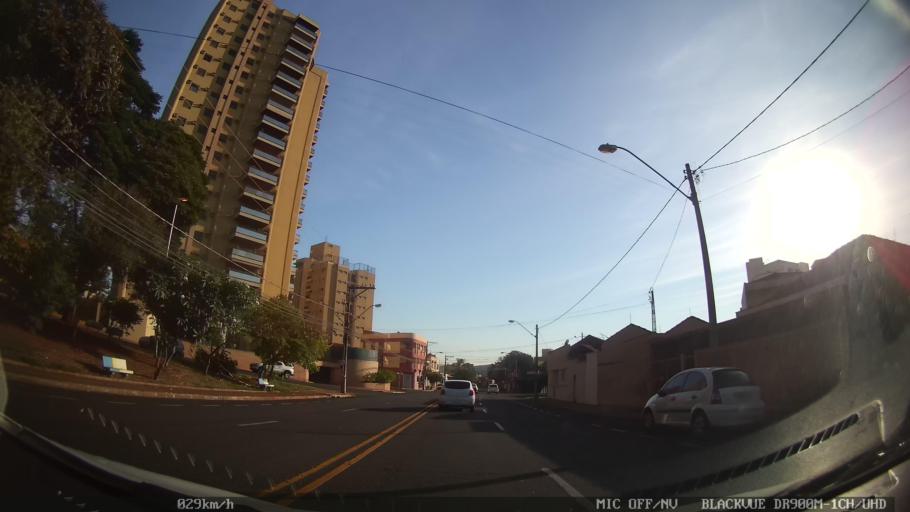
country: BR
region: Sao Paulo
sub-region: Ribeirao Preto
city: Ribeirao Preto
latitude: -21.1889
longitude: -47.8012
